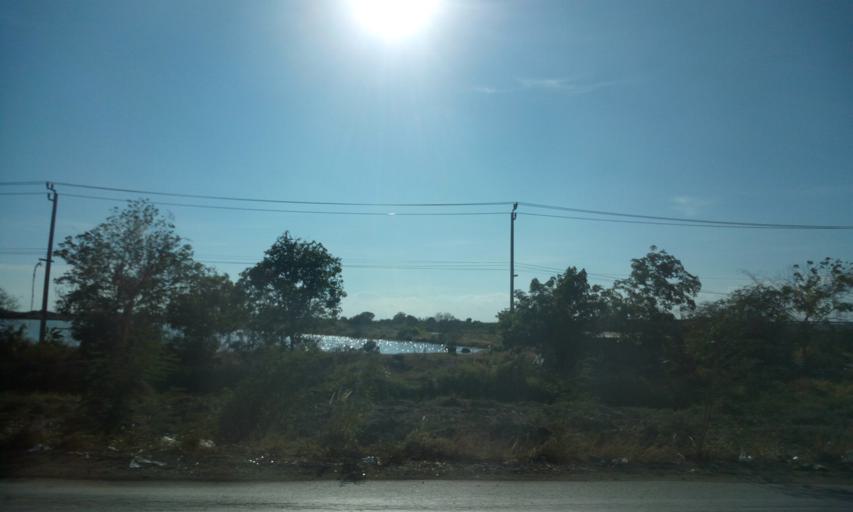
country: TH
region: Samut Prakan
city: Bang Bo District
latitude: 13.5682
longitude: 100.7556
